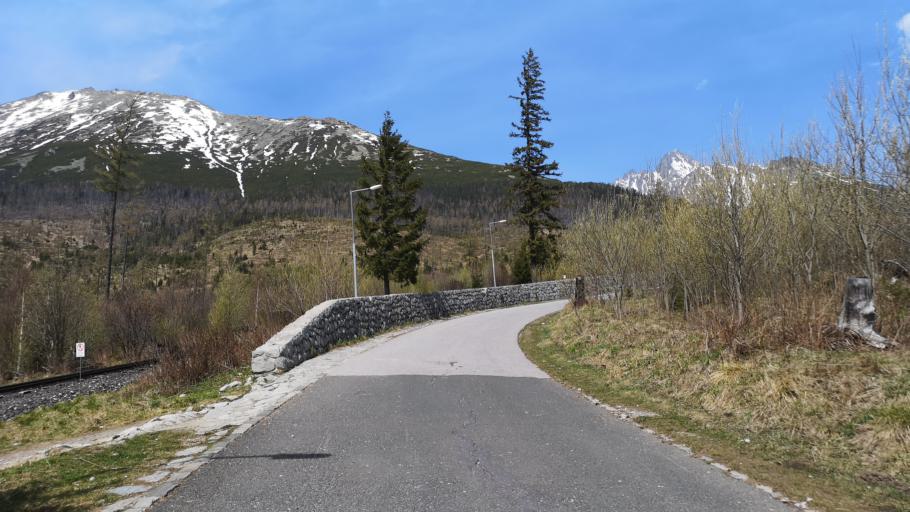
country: SK
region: Presovsky
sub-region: Okres Poprad
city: Vysoke Tatry
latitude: 49.1491
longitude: 20.2231
